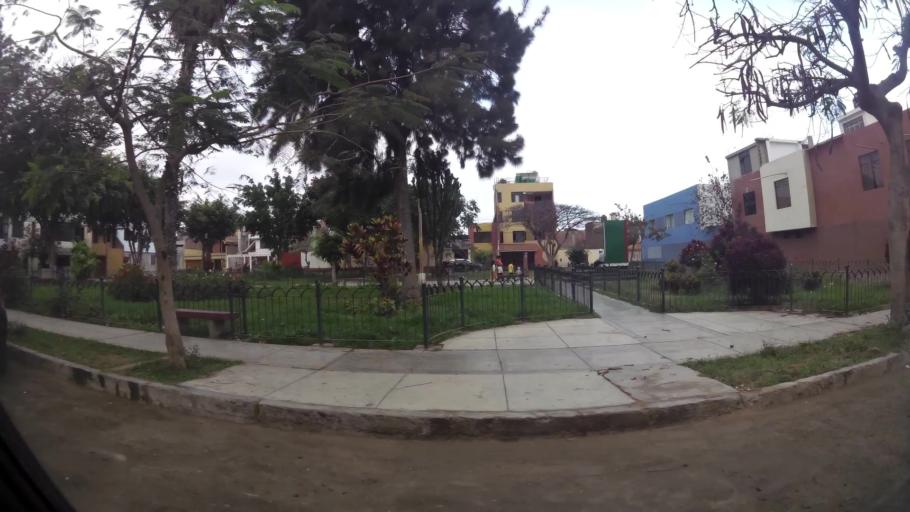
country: PE
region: La Libertad
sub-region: Provincia de Trujillo
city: Trujillo
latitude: -8.0961
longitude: -79.0208
